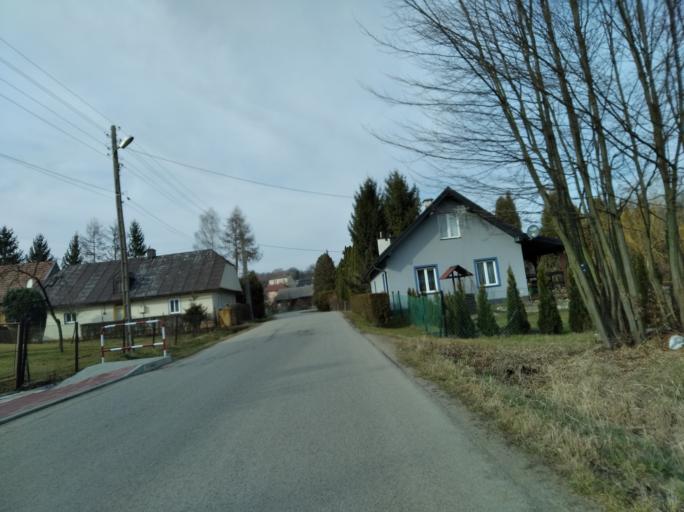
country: PL
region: Subcarpathian Voivodeship
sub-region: Powiat brzozowski
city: Turze Pole
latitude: 49.6628
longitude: 22.0032
